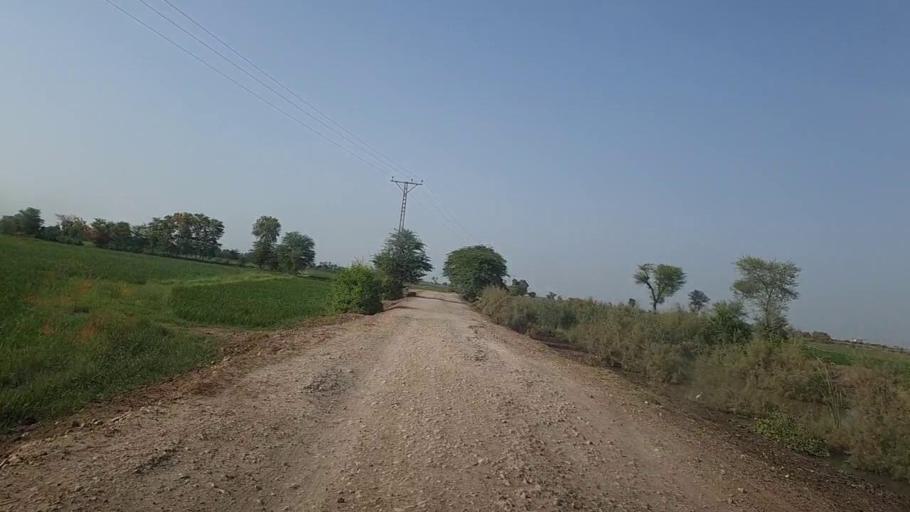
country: PK
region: Sindh
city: Sita Road
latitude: 27.1043
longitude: 67.8744
